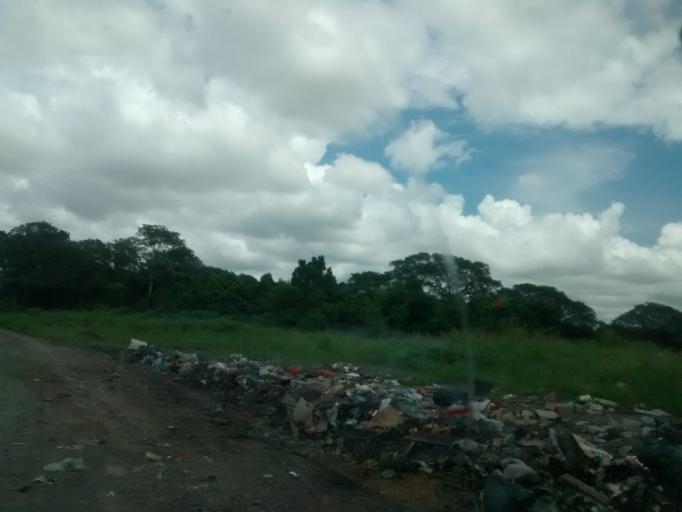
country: AR
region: Chaco
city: Fontana
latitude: -27.4149
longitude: -58.9845
